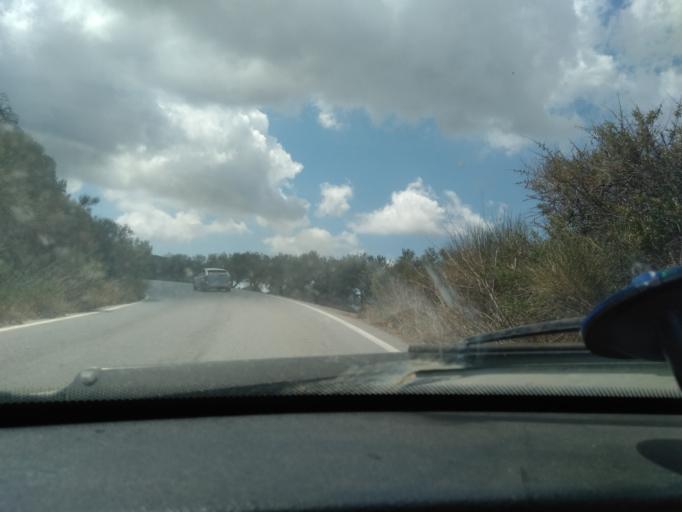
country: GR
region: Crete
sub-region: Nomos Lasithiou
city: Siteia
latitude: 35.0976
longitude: 26.0714
